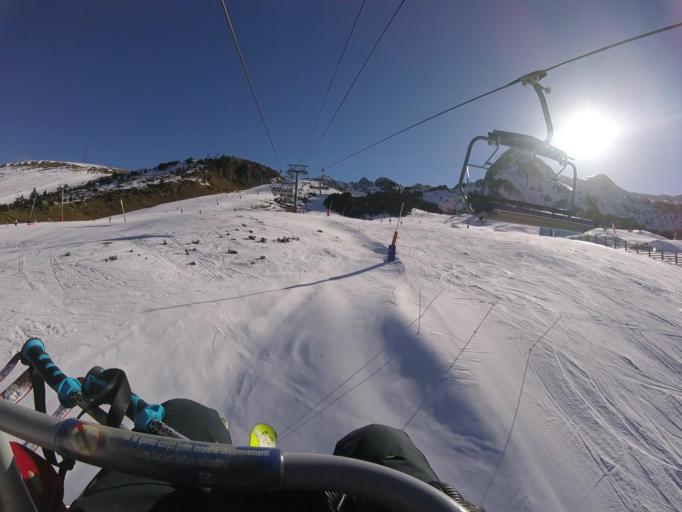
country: AD
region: Encamp
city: Pas de la Casa
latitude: 42.5293
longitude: 1.6994
